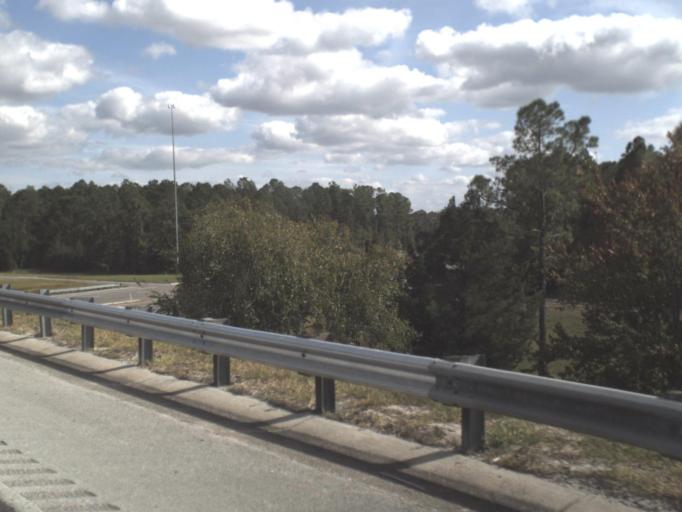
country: US
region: Florida
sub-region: Orange County
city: Christmas
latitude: 28.4525
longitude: -80.9798
